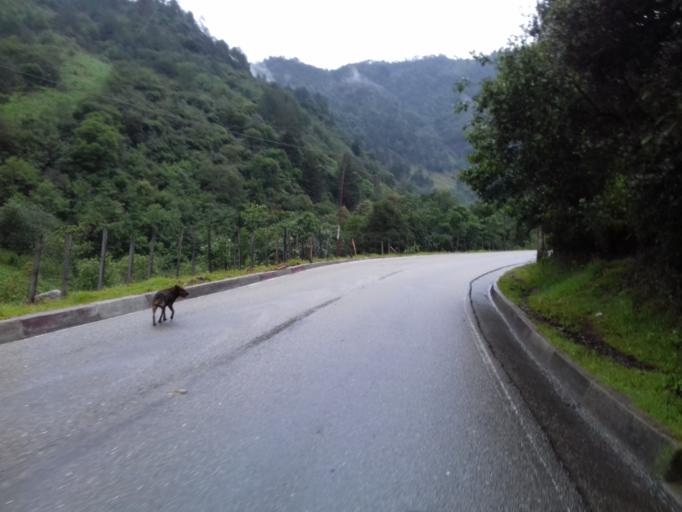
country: GT
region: Quiche
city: Nebaj
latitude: 15.3867
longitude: -91.1135
